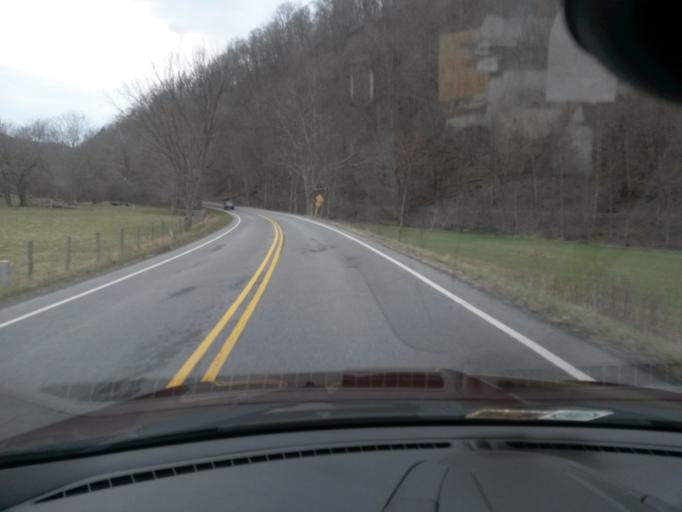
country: US
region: Virginia
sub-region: Highland County
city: Monterey
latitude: 38.2957
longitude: -79.6627
